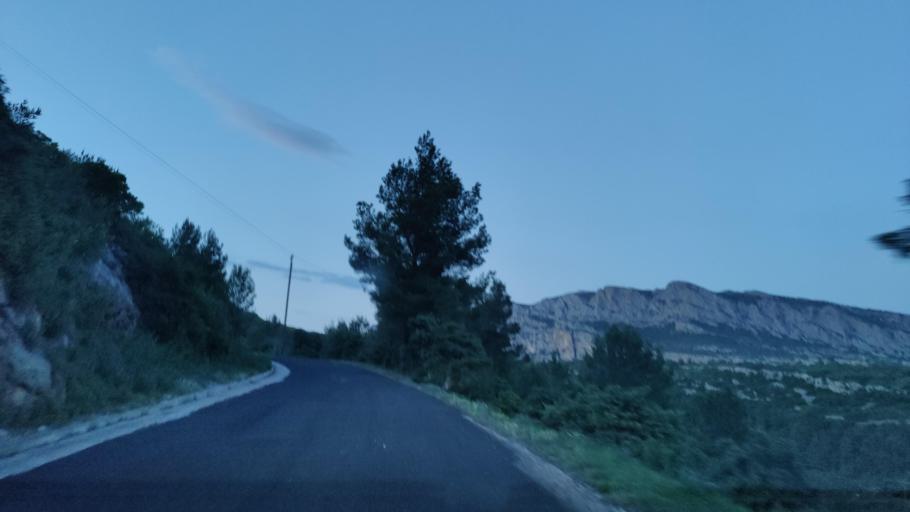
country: FR
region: Languedoc-Roussillon
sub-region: Departement des Pyrenees-Orientales
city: Estagel
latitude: 42.8540
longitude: 2.7680
